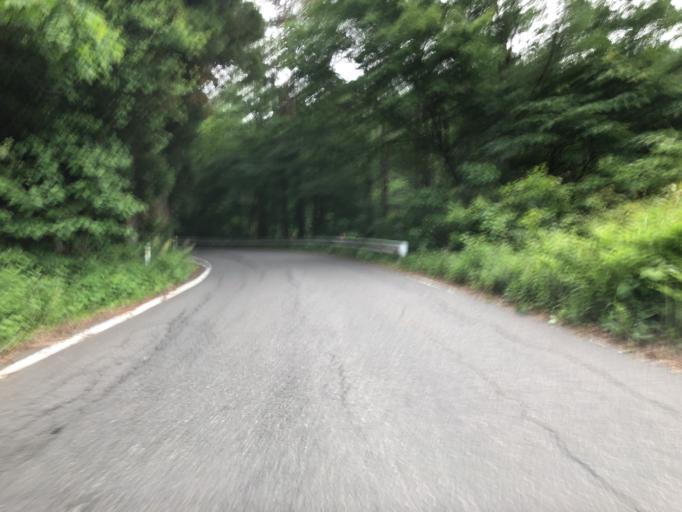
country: JP
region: Fukushima
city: Funehikimachi-funehiki
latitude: 37.3884
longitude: 140.7042
